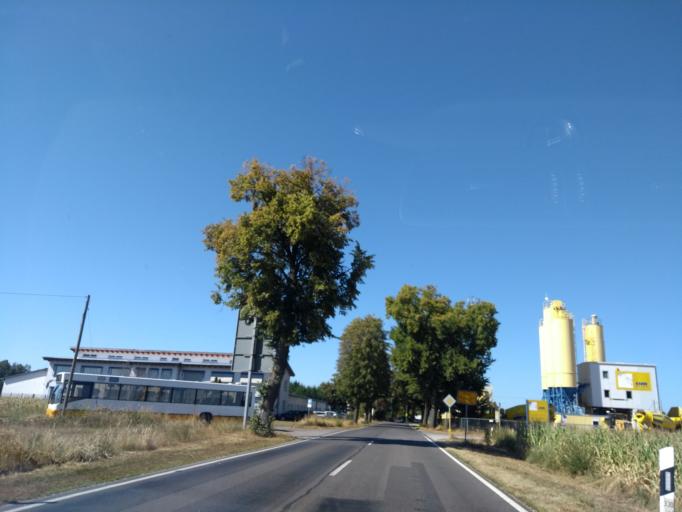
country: DE
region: Brandenburg
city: Lubbenau
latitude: 51.8389
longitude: 13.9756
